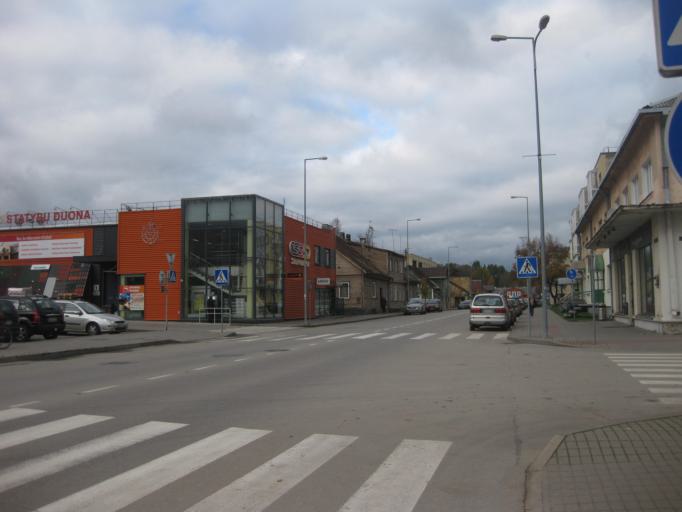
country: LT
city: Prienai
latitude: 54.6357
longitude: 23.9459
